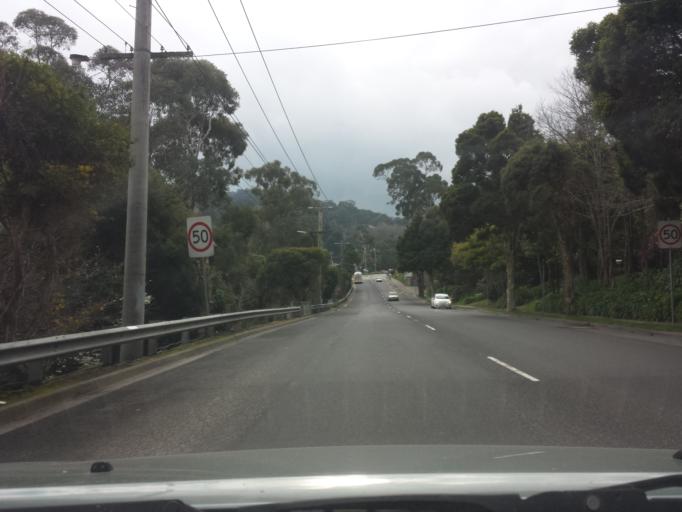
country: AU
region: Victoria
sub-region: Yarra Ranges
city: Belgrave Heights
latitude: -37.9109
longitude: 145.3570
